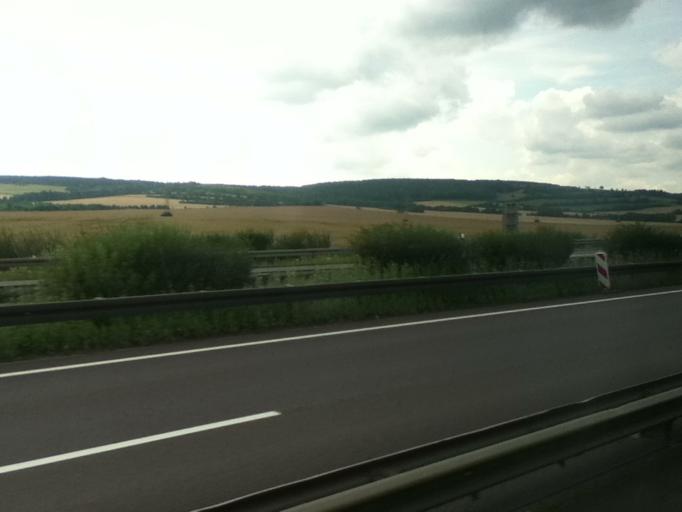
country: DE
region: Thuringia
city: Seebergen
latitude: 50.8789
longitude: 10.8035
